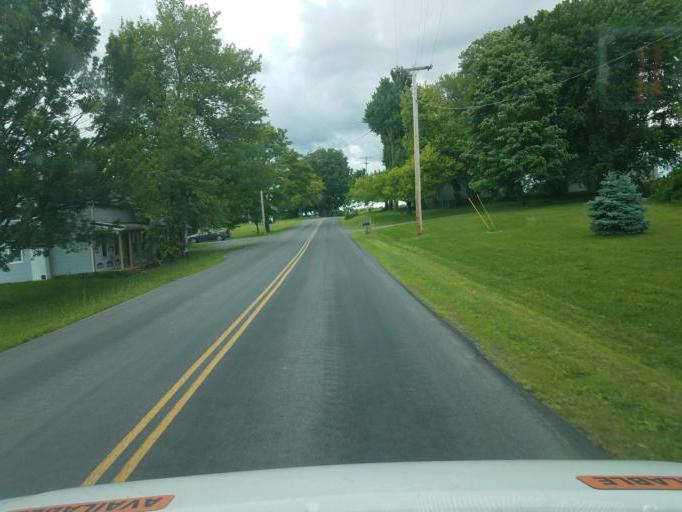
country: US
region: New York
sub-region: Seneca County
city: Waterloo
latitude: 42.9705
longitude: -76.9417
